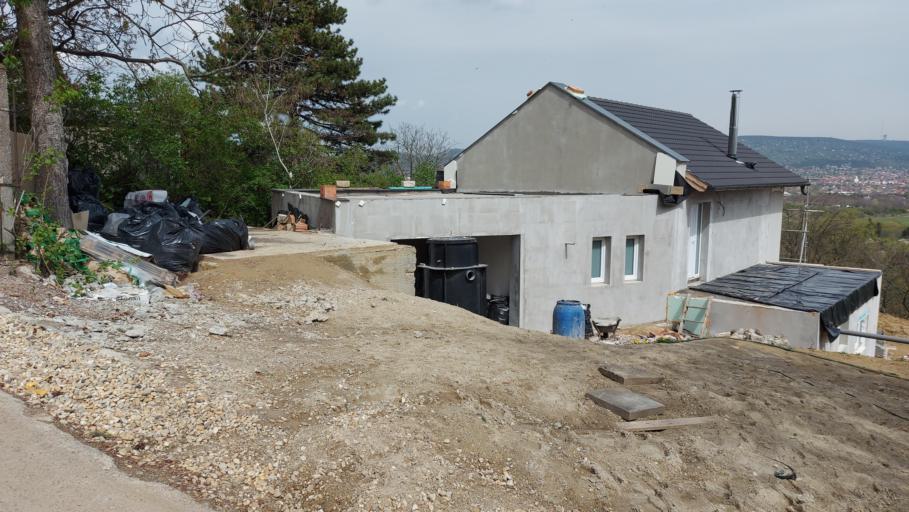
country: HU
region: Pest
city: Diosd
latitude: 47.4344
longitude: 18.9503
